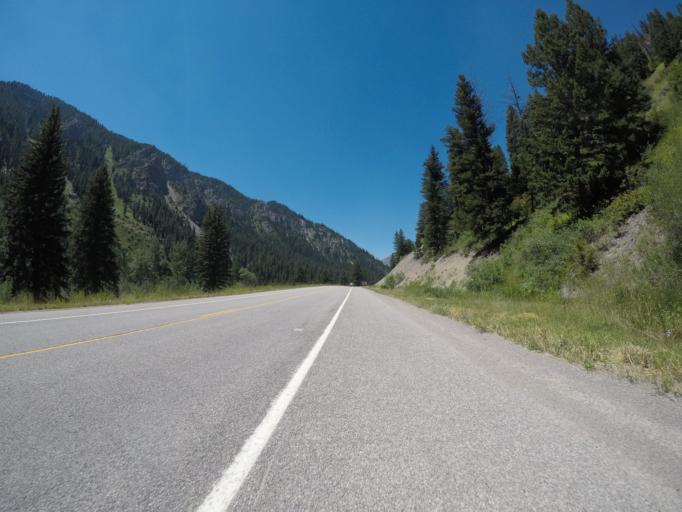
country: US
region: Wyoming
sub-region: Teton County
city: Hoback
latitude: 43.1970
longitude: -110.8849
